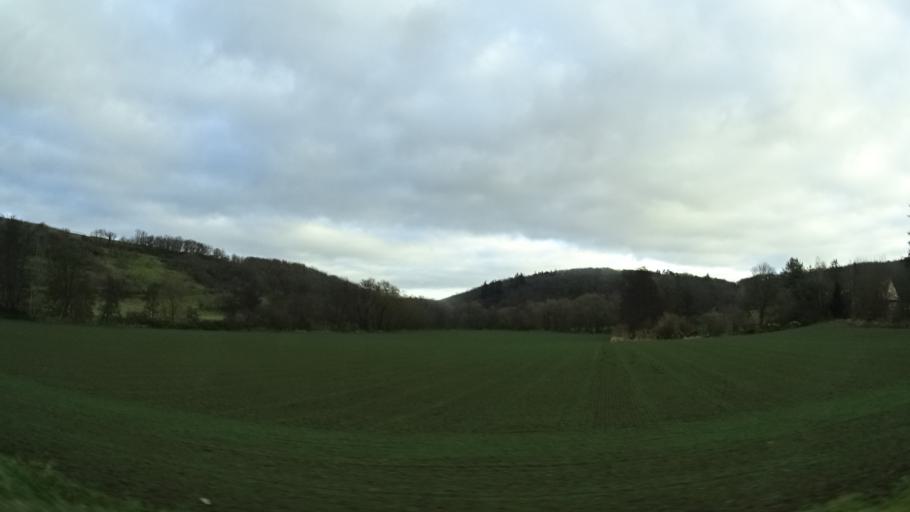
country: DE
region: Rheinland-Pfalz
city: Furfeld
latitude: 49.7736
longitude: 7.9236
